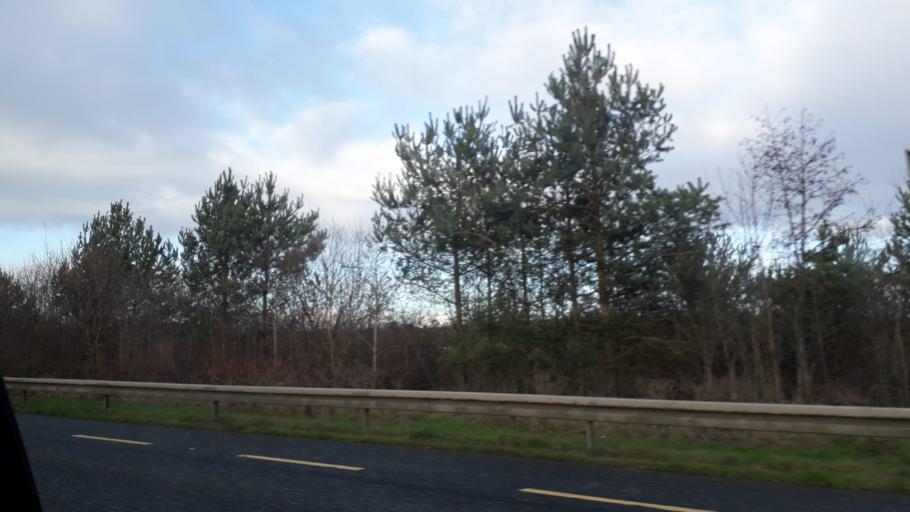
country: IE
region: Ulster
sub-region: County Monaghan
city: Carrickmacross
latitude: 53.9879
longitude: -6.7154
